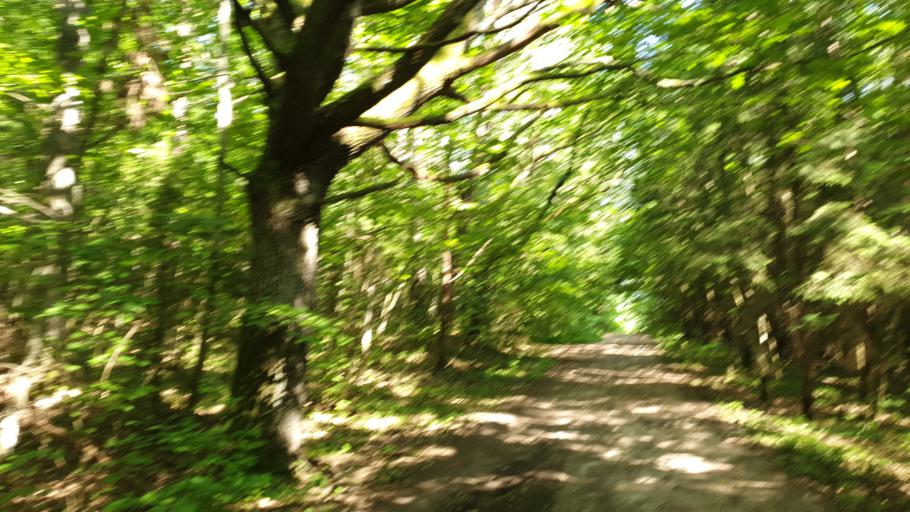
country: LT
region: Vilnius County
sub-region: Vilnius
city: Fabijoniskes
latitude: 54.7889
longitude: 25.3141
